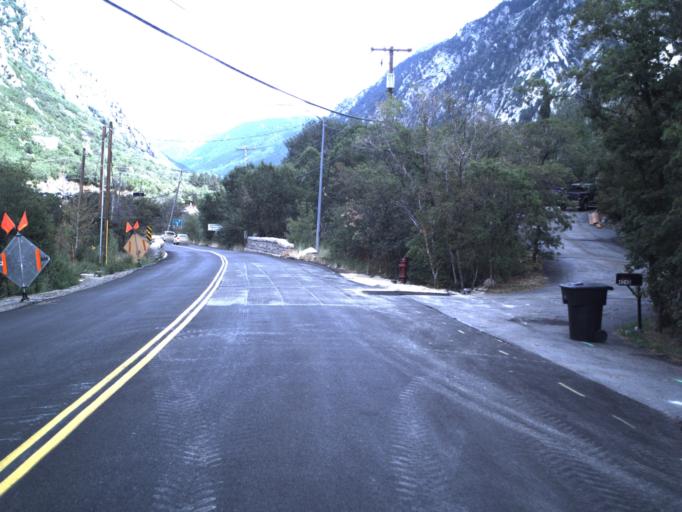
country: US
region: Utah
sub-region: Salt Lake County
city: Granite
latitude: 40.5723
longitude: -111.7794
